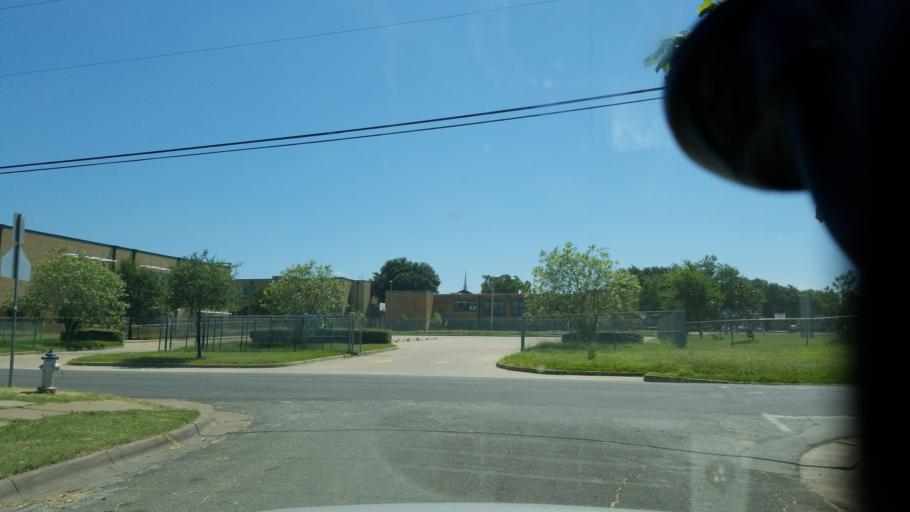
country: US
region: Texas
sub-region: Dallas County
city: Cockrell Hill
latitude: 32.7084
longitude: -96.8249
